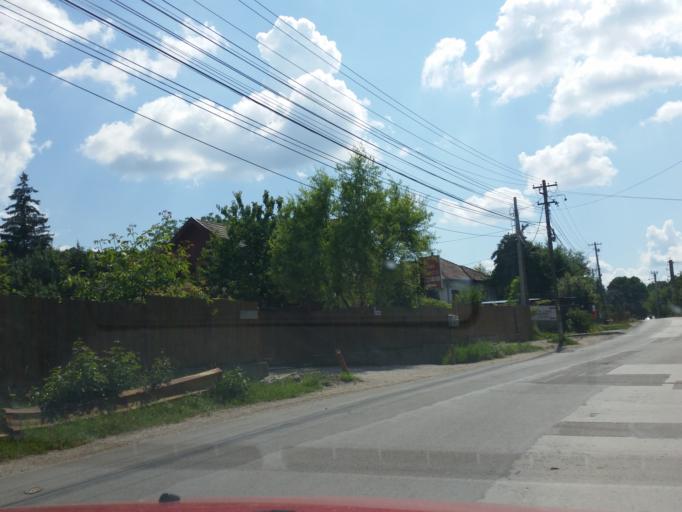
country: RO
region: Cluj
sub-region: Comuna Feleacu
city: Feleacu
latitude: 46.7280
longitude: 23.5860
